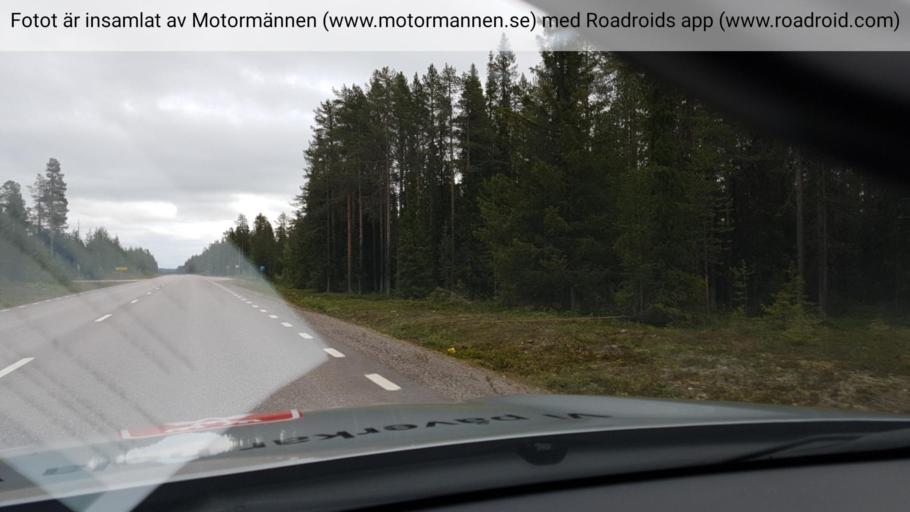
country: SE
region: Norrbotten
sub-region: Gallivare Kommun
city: Gaellivare
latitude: 67.0810
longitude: 21.0555
